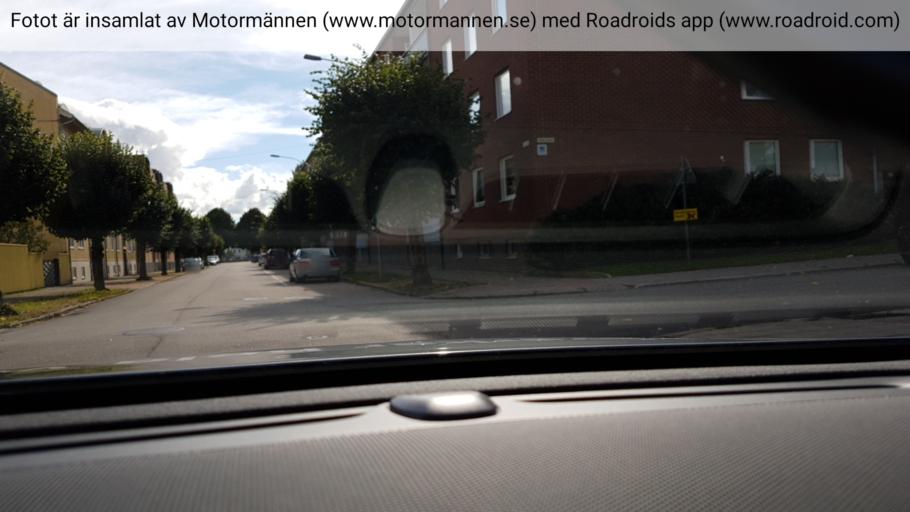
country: SE
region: Vaestra Goetaland
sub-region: Vanersborgs Kommun
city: Vanersborg
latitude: 58.3780
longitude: 12.3257
